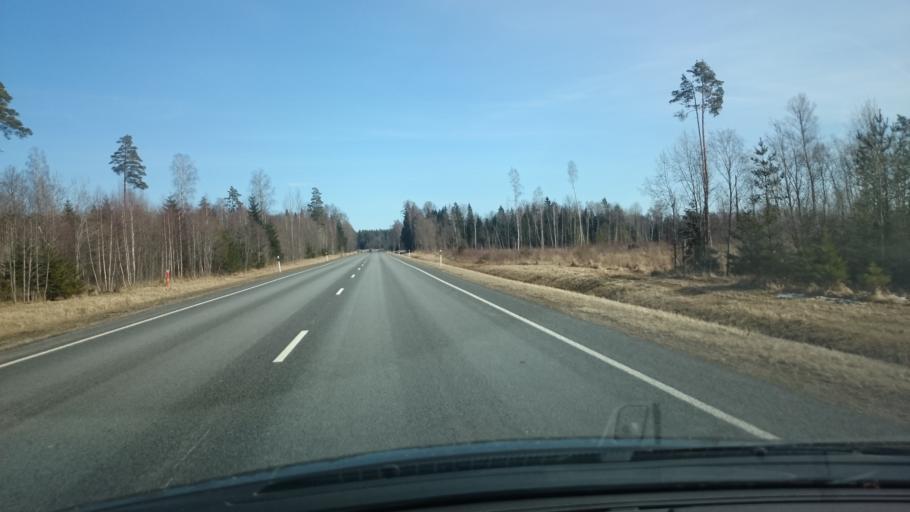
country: EE
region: Paernumaa
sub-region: Vaendra vald (alev)
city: Vandra
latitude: 58.6687
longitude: 25.0663
